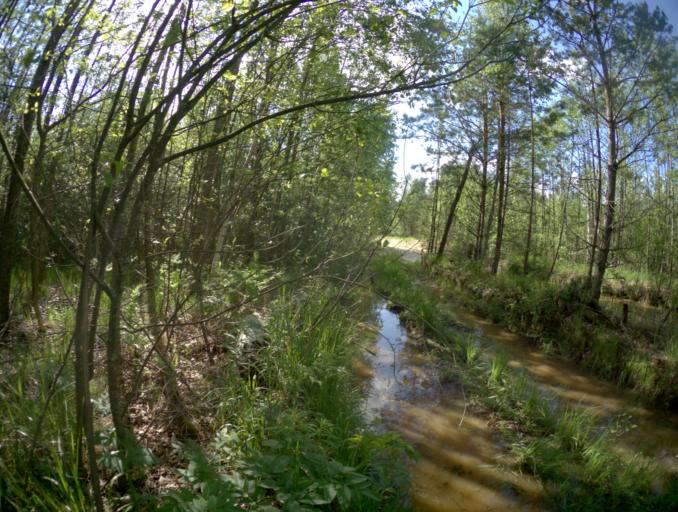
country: RU
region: Vladimir
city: Zolotkovo
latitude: 55.3315
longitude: 40.9903
